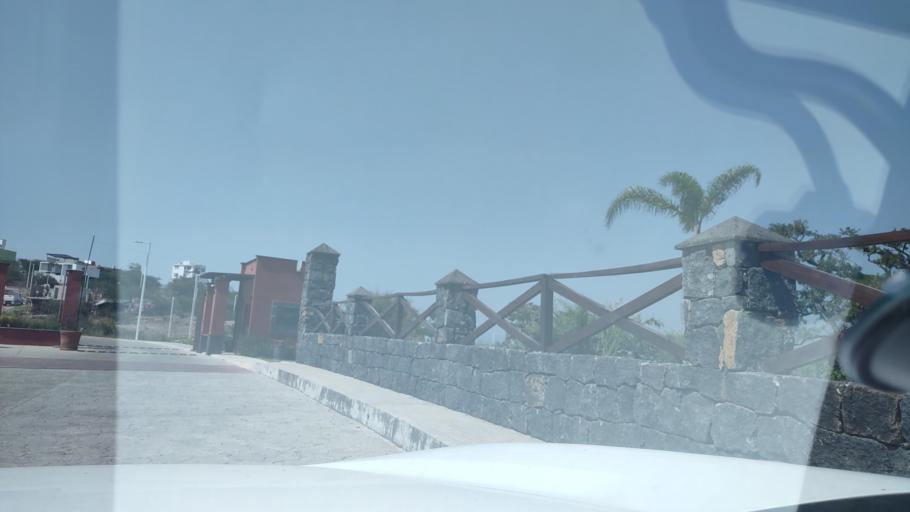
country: MX
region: Veracruz
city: El Castillo
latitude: 19.5259
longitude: -96.8688
